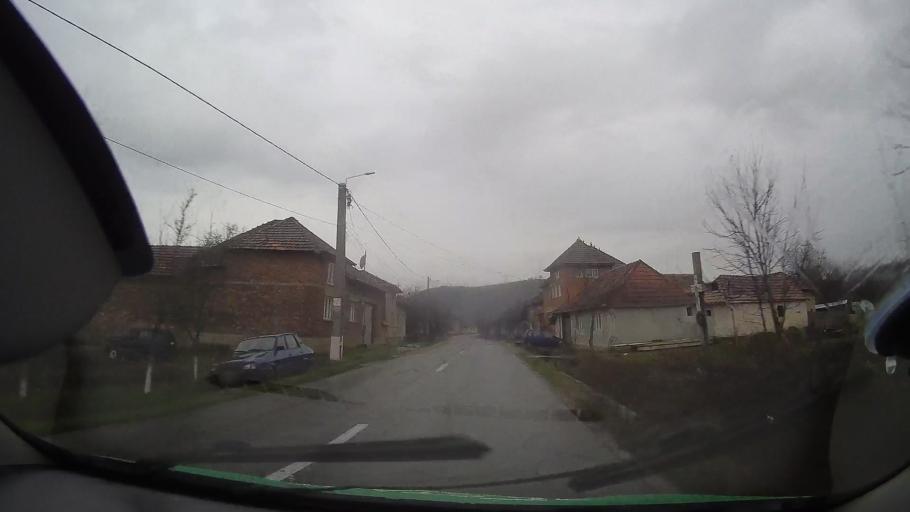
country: RO
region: Bihor
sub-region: Comuna Pocola
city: Pocola
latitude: 46.6900
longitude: 22.2697
